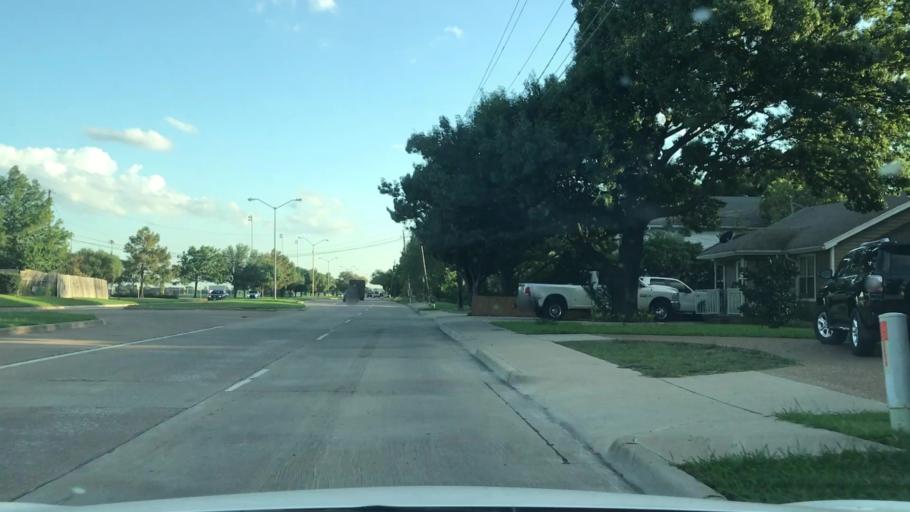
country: US
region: Texas
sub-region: Dallas County
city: Mesquite
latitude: 32.8165
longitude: -96.6655
